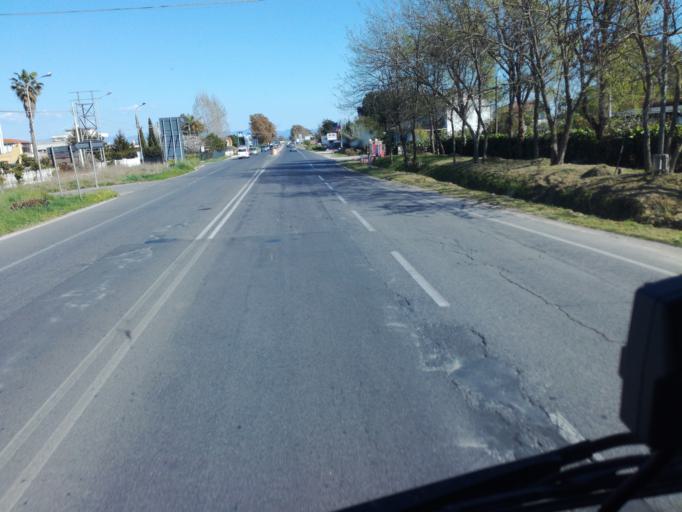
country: IT
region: Latium
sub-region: Provincia di Latina
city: Latina
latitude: 41.4385
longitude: 12.9168
